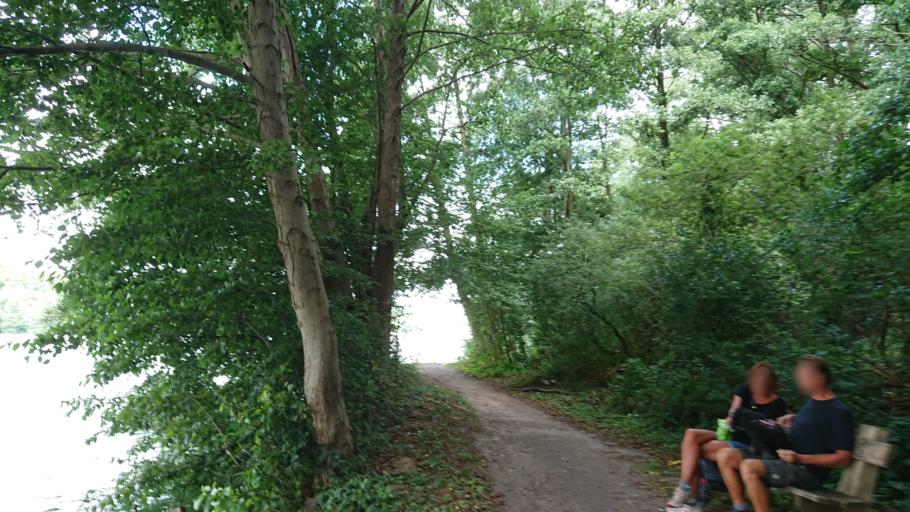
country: DE
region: Schleswig-Holstein
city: Schmilau
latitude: 53.6792
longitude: 10.7591
